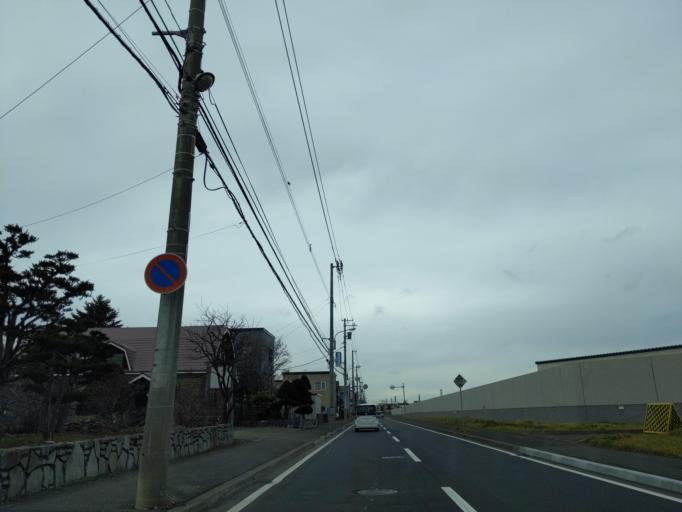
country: JP
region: Hokkaido
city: Sapporo
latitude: 43.0829
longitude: 141.3944
